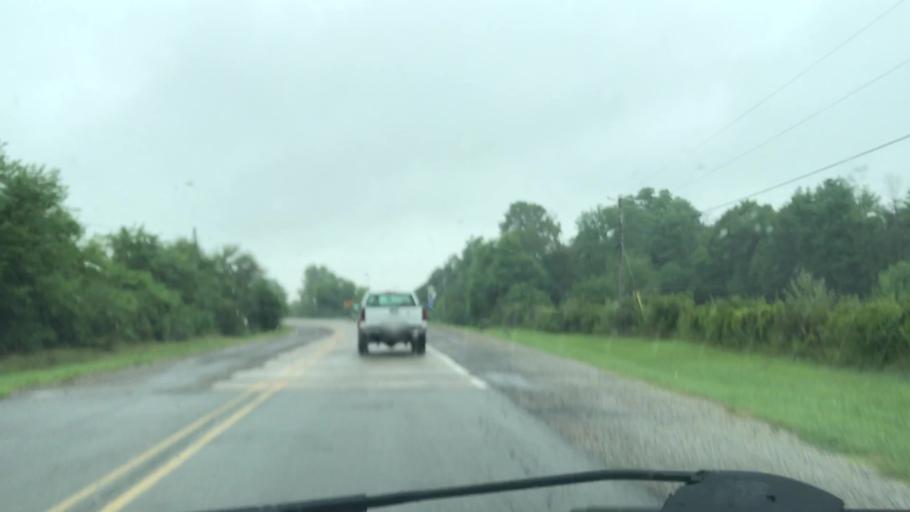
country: US
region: Indiana
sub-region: Boone County
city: Lebanon
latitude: 40.0652
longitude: -86.4929
